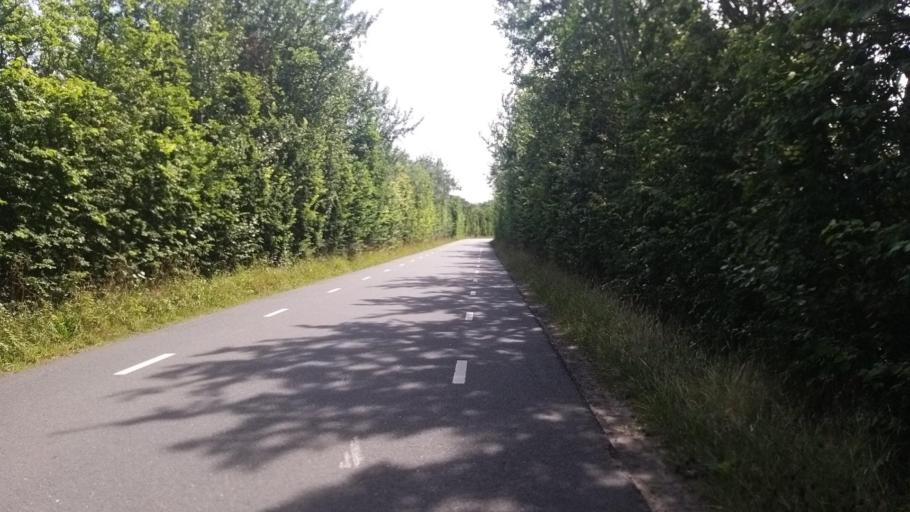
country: NL
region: North Holland
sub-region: Gemeente Texel
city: Den Burg
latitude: 53.0872
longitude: 4.7832
